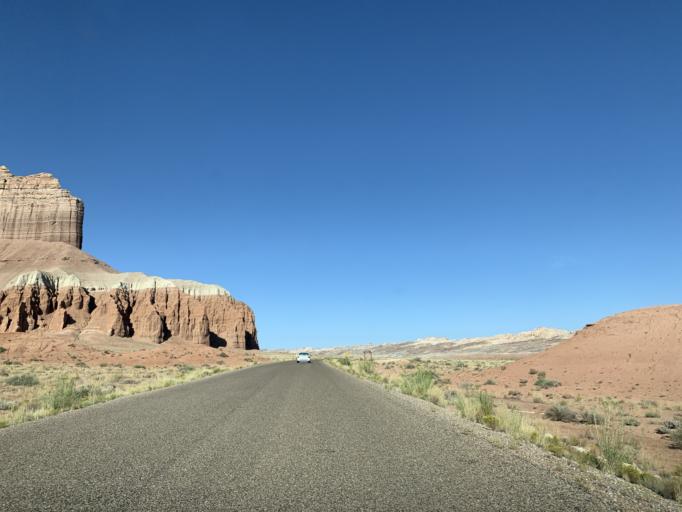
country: US
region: Utah
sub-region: Emery County
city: Ferron
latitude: 38.5831
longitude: -110.7124
